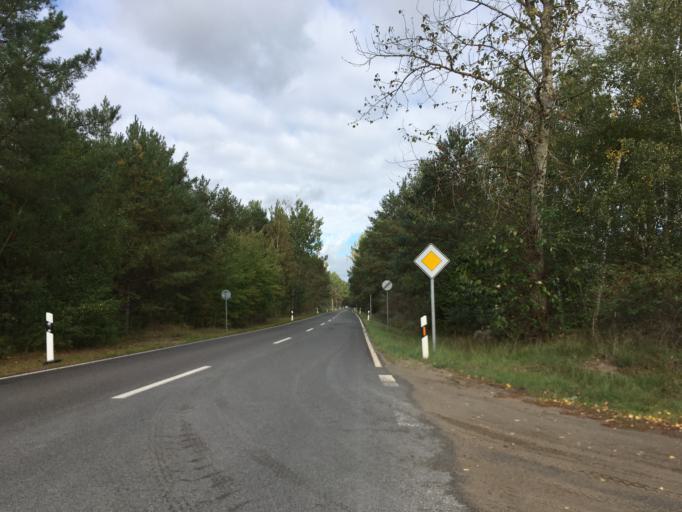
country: PL
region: West Pomeranian Voivodeship
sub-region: Powiat gryfinski
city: Cedynia
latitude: 52.8926
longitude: 14.1311
